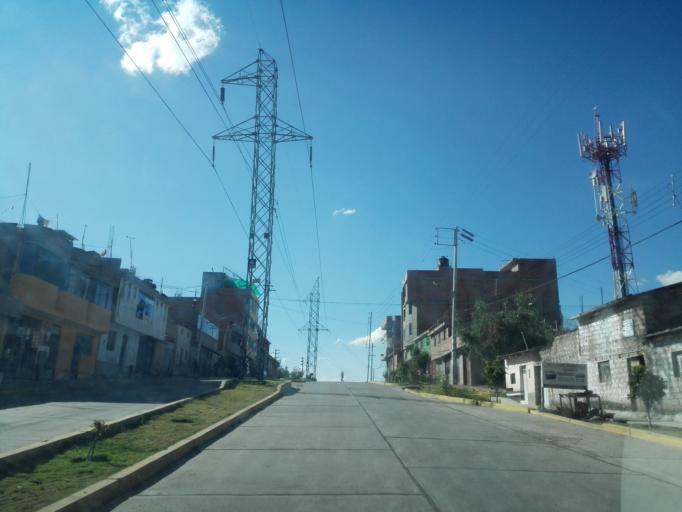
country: PE
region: Ayacucho
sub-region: Provincia de Huamanga
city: Ayacucho
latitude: -13.1478
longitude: -74.2149
